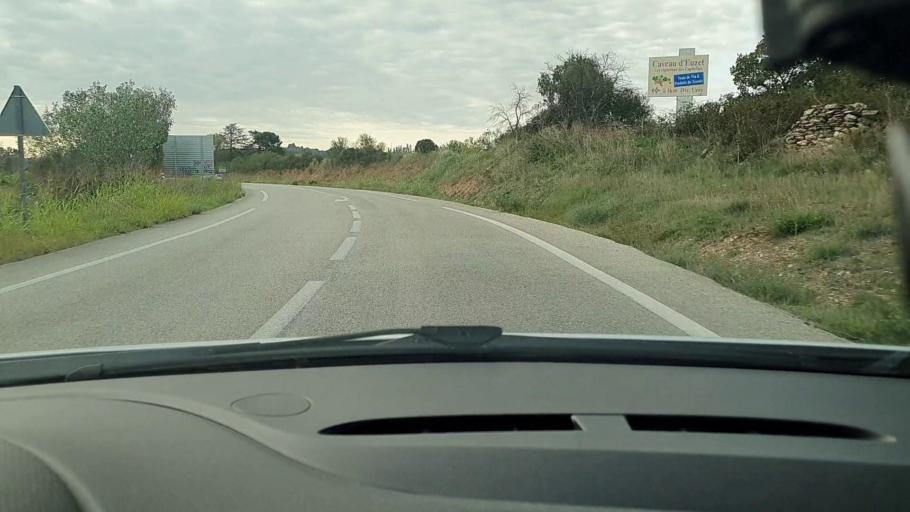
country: FR
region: Languedoc-Roussillon
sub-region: Departement du Gard
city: Mons
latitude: 44.0751
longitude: 4.2193
